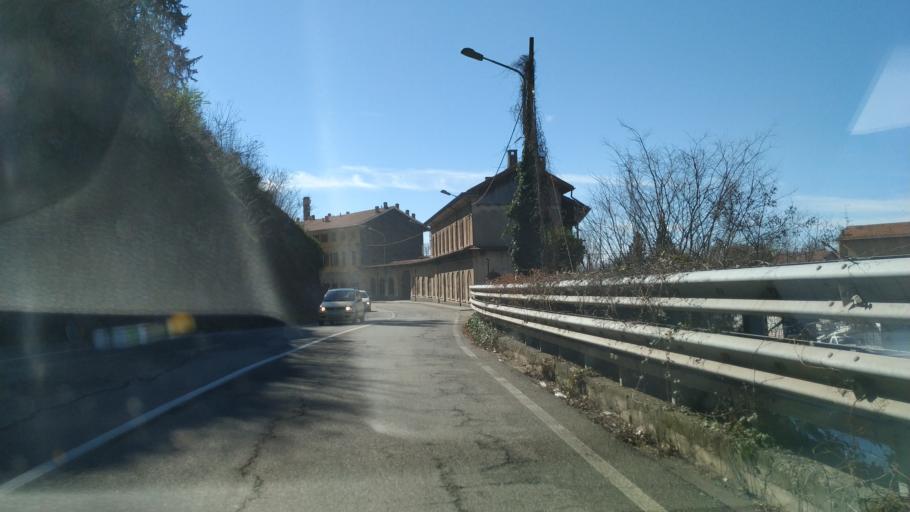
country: IT
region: Piedmont
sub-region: Provincia di Novara
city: Romagnano Sesia
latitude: 45.6365
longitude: 8.3785
